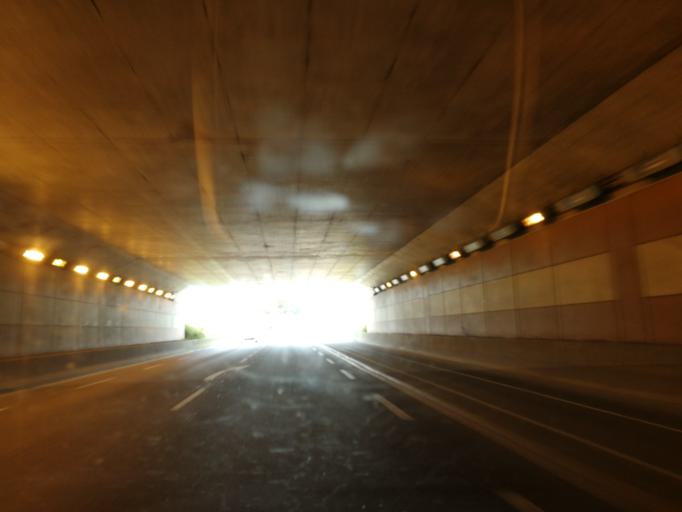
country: FR
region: Midi-Pyrenees
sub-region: Departement de la Haute-Garonne
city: Cornebarrieu
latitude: 43.6455
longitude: 1.3538
